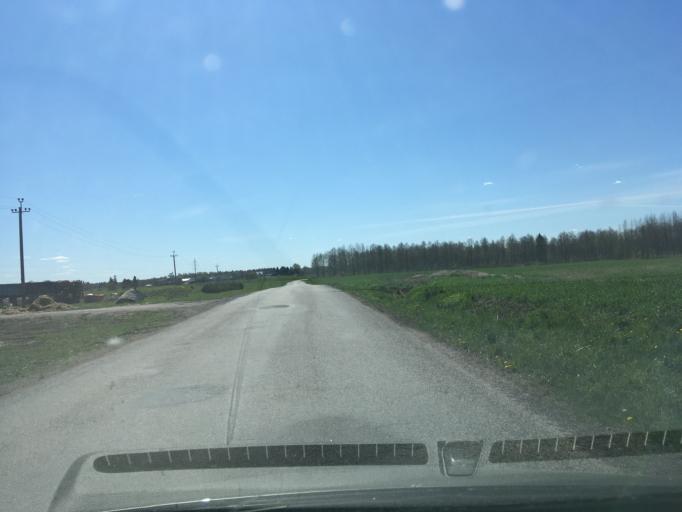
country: EE
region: Harju
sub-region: Raasiku vald
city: Arukula
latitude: 59.3893
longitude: 25.0806
